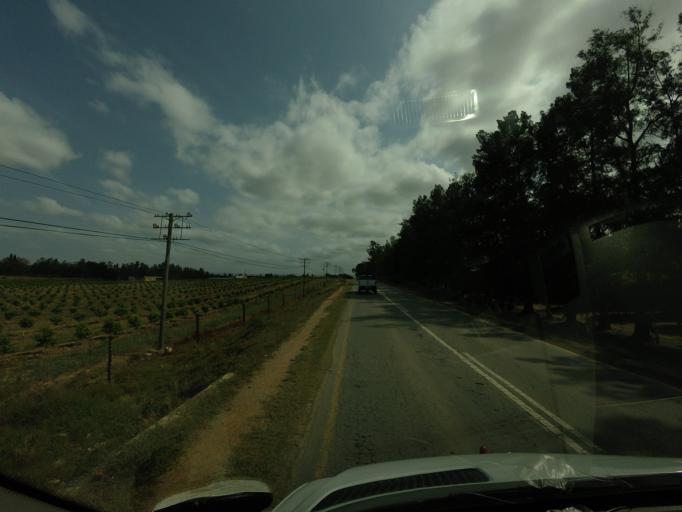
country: ZA
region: Eastern Cape
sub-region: Cacadu District Municipality
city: Kirkwood
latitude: -33.5292
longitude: 25.6915
